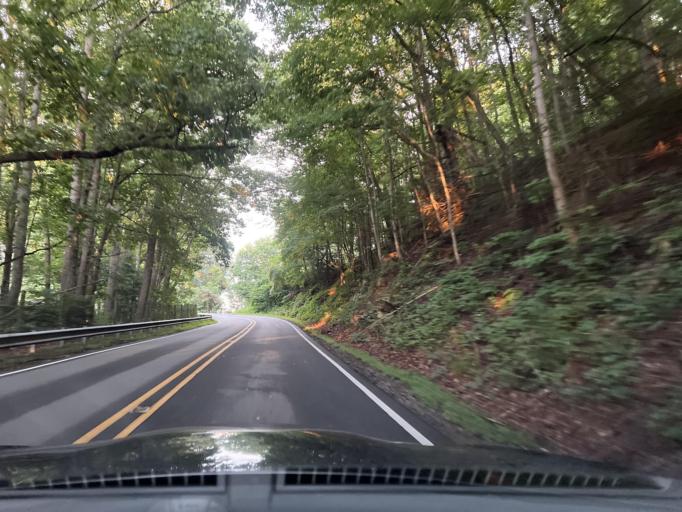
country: US
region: North Carolina
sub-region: Buncombe County
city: Asheville
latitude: 35.6068
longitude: -82.5383
